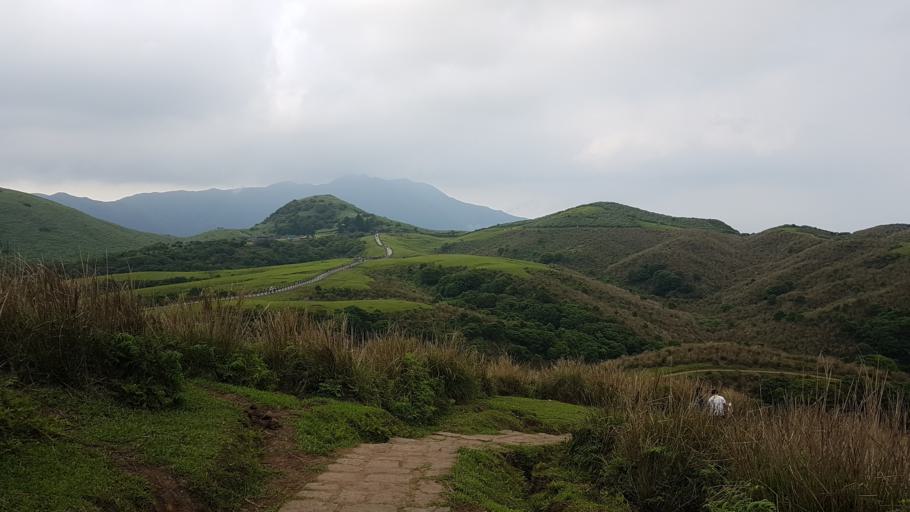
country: TW
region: Taipei
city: Taipei
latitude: 25.1615
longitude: 121.5763
